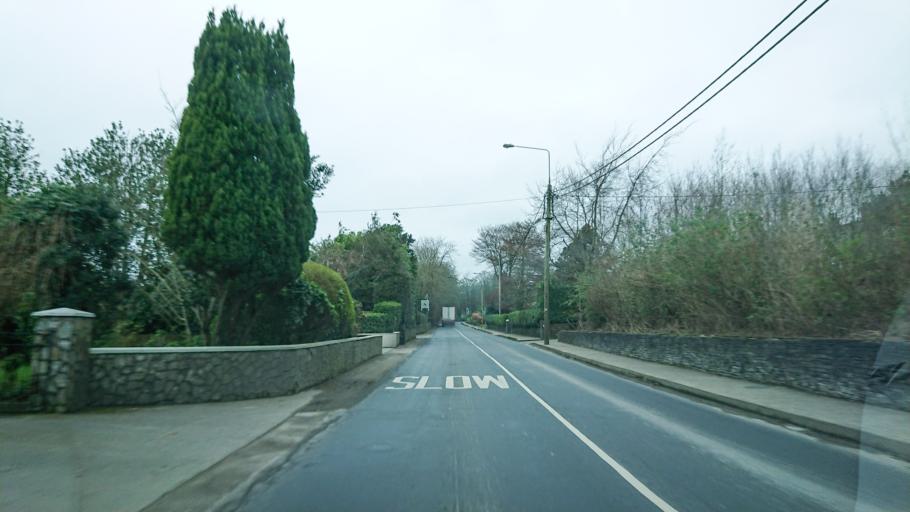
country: IE
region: Munster
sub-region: County Cork
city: Bandon
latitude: 51.7479
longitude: -8.7426
